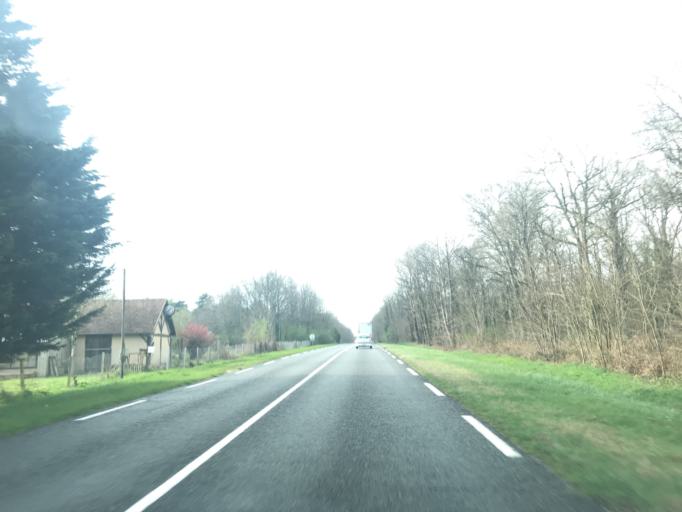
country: FR
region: Centre
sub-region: Departement du Loiret
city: Nevoy
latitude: 47.7320
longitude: 2.5736
